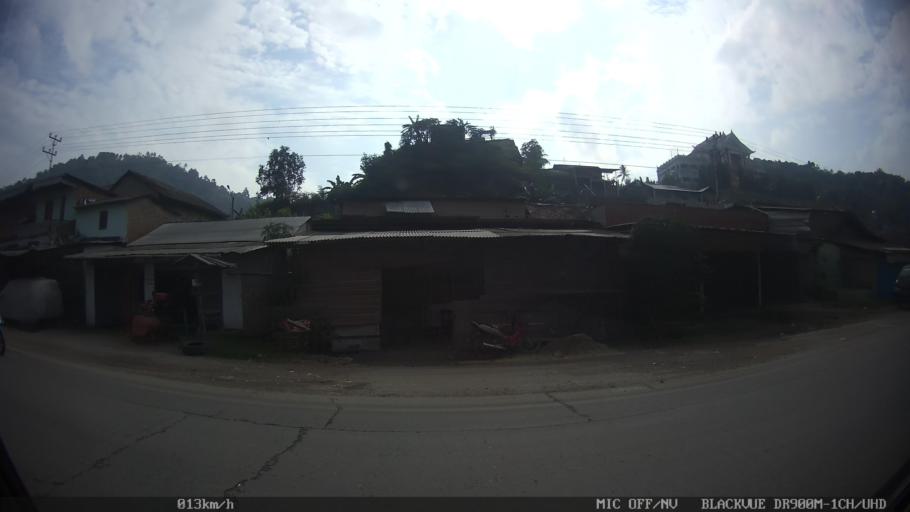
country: ID
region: Lampung
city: Panjang
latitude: -5.4640
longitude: 105.3216
